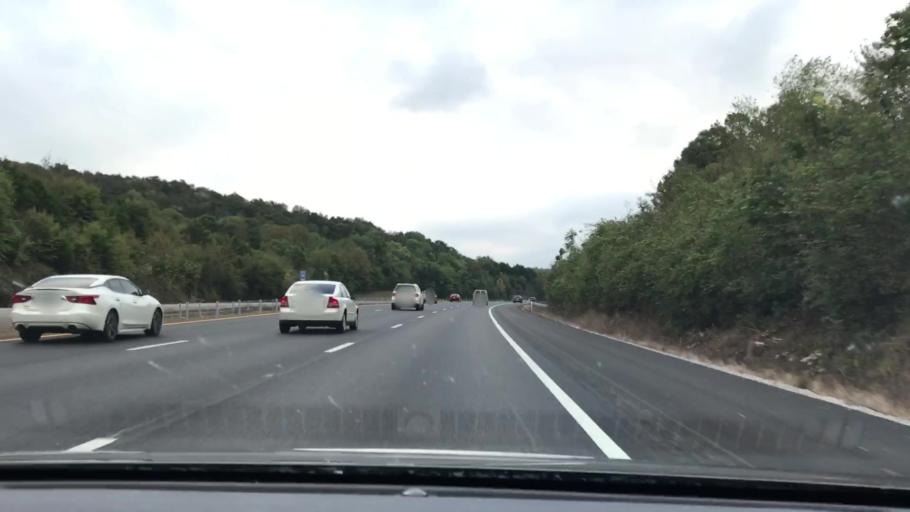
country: US
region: Tennessee
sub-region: Wilson County
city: Watertown
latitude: 36.1737
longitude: -86.0823
